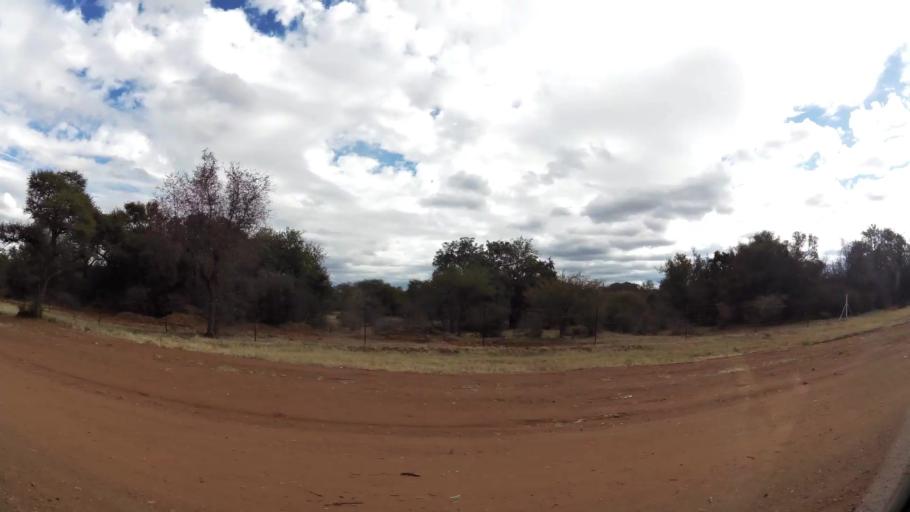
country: ZA
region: Limpopo
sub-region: Waterberg District Municipality
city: Warmbaths
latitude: -24.8998
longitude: 28.2802
